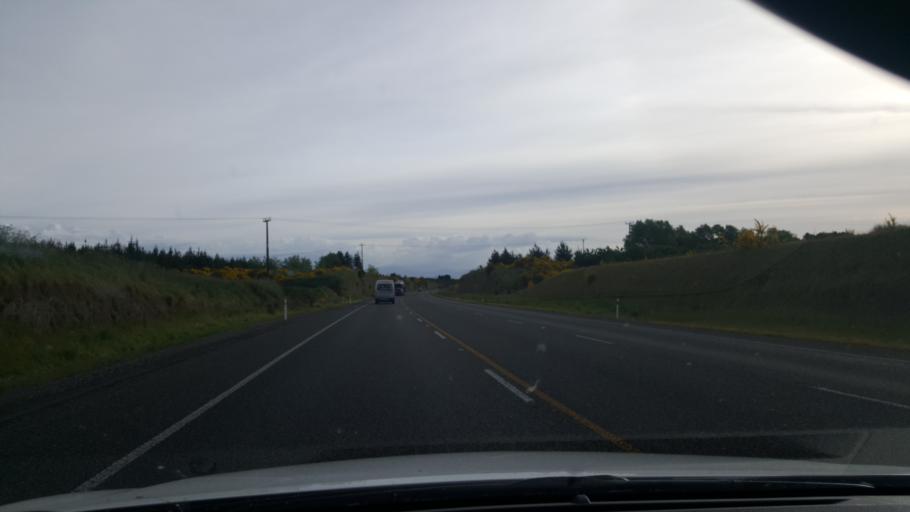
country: NZ
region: Waikato
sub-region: Taupo District
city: Taupo
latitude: -38.7193
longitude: 176.1024
